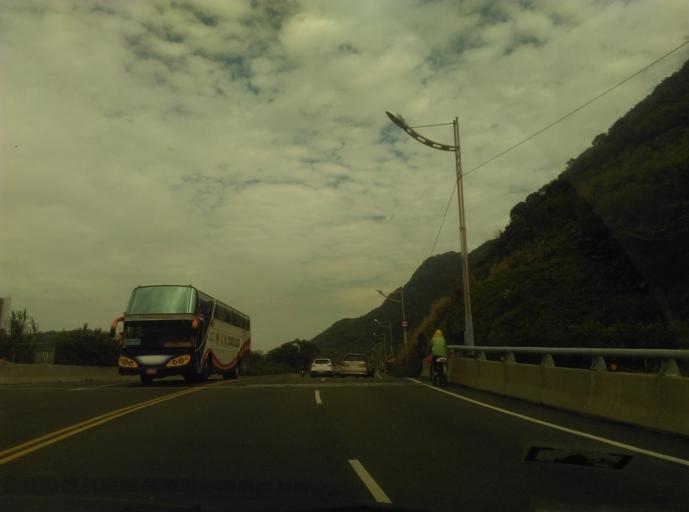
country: TW
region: Taiwan
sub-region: Keelung
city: Keelung
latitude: 25.1592
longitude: 121.6981
